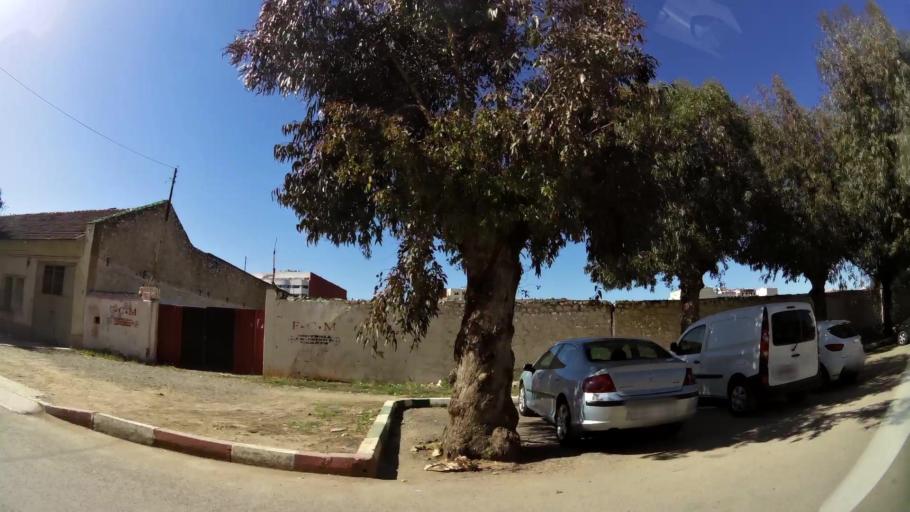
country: MA
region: Meknes-Tafilalet
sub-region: Meknes
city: Meknes
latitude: 33.8949
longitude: -5.5382
